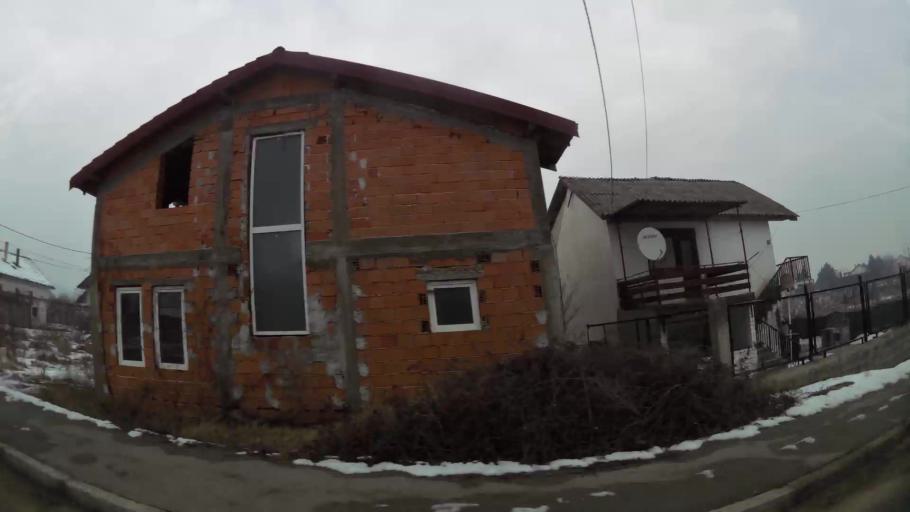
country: MK
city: Kondovo
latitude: 42.0359
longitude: 21.3414
